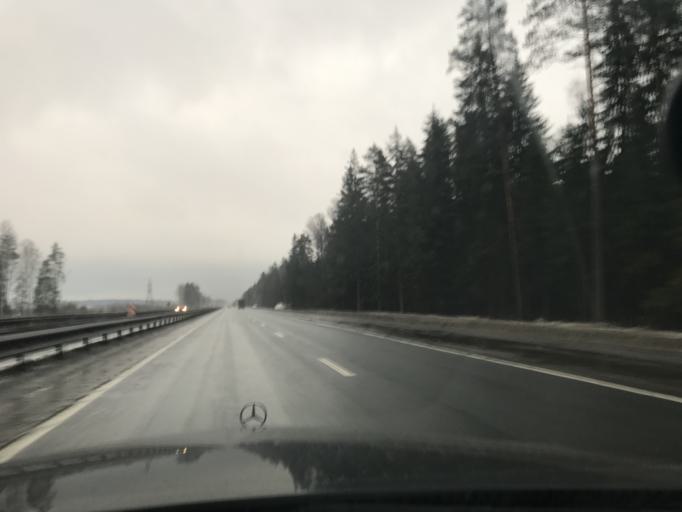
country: RU
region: Vladimir
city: Krasnyy Oktyabr'
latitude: 56.2183
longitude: 41.4594
